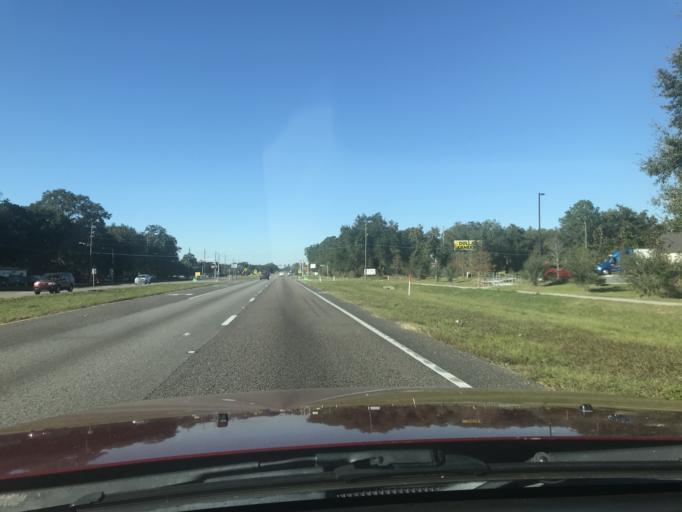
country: US
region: Florida
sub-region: Osceola County
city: Campbell
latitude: 28.2570
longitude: -81.4593
